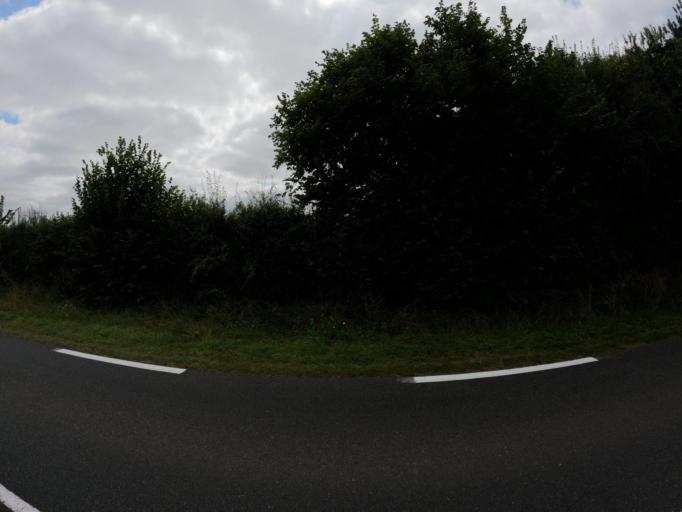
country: FR
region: Poitou-Charentes
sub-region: Departement de la Vienne
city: Savigne
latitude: 46.1592
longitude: 0.3499
